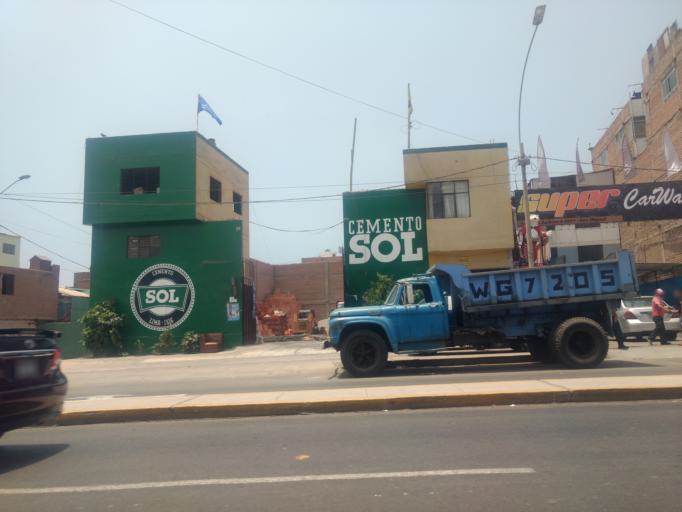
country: PE
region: Callao
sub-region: Callao
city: Callao
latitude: -12.0637
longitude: -77.0822
